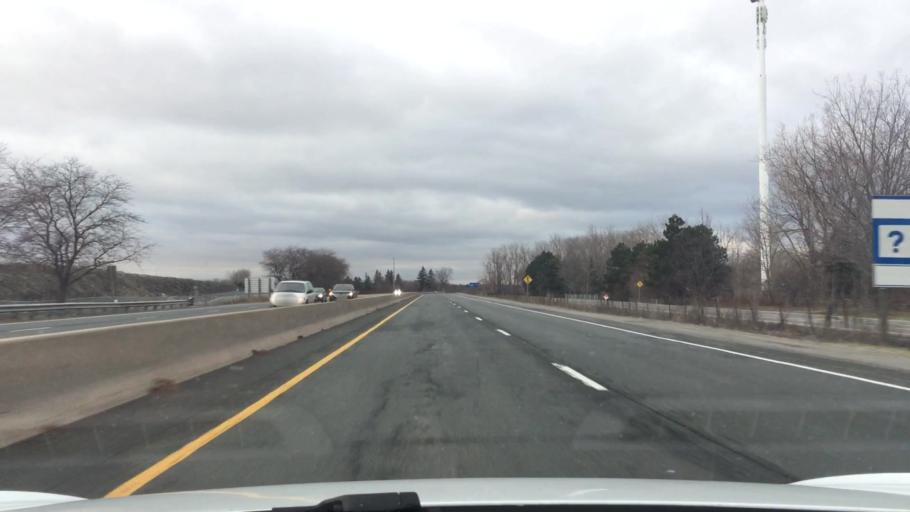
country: US
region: New York
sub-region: Niagara County
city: Lewiston
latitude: 43.1509
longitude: -79.0804
